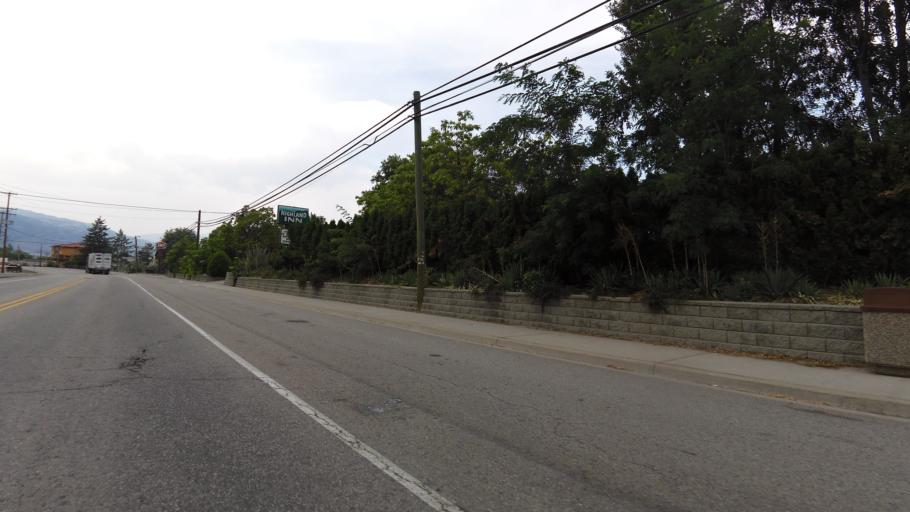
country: CA
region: British Columbia
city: Osoyoos
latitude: 49.0285
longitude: -119.4447
